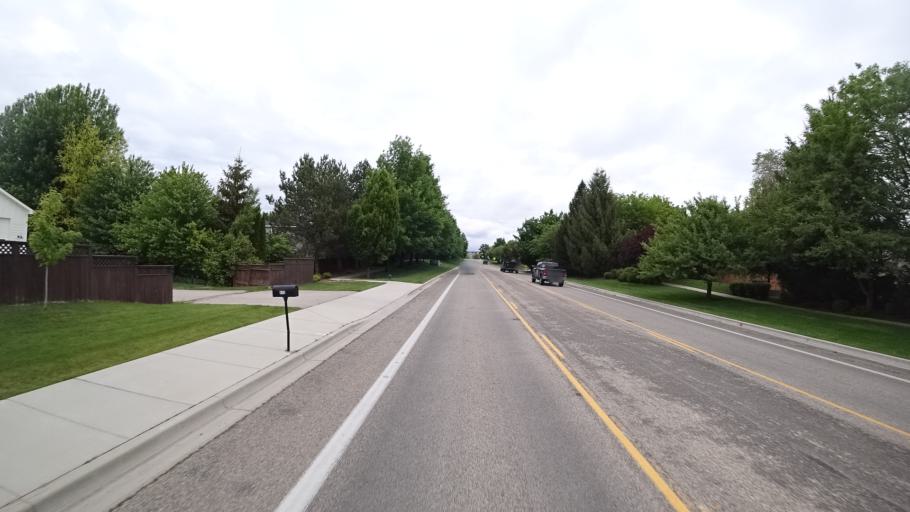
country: US
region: Idaho
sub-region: Ada County
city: Eagle
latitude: 43.7065
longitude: -116.3480
